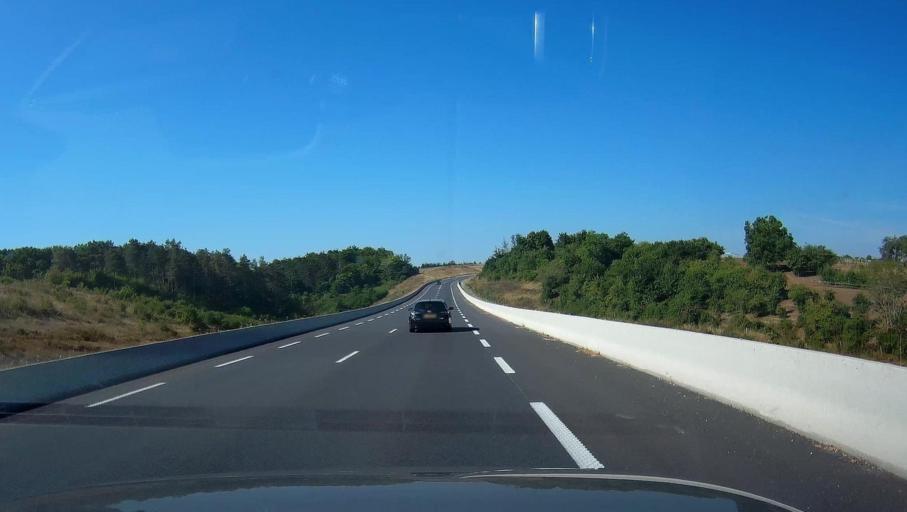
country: FR
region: Lorraine
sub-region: Departement de Meurthe-et-Moselle
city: Colombey-les-Belles
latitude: 48.5510
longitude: 5.9169
